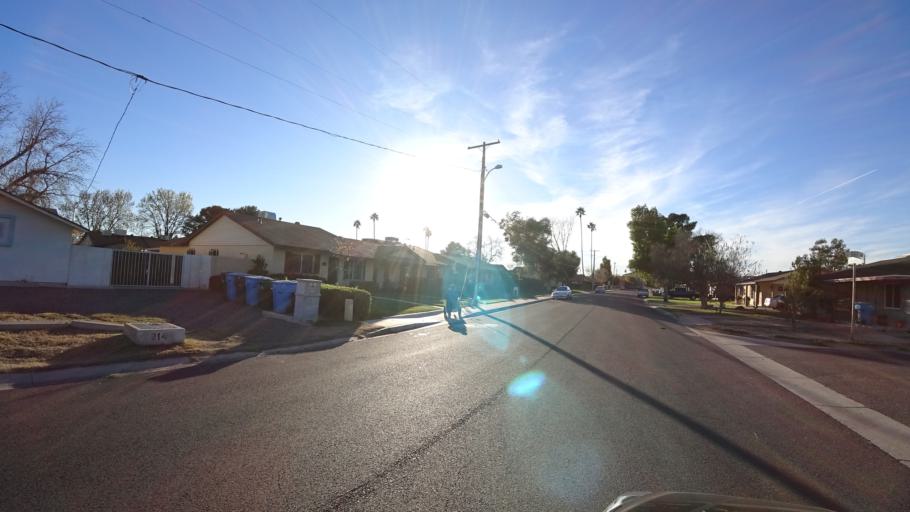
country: US
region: Arizona
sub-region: Maricopa County
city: Phoenix
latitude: 33.4769
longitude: -112.1064
